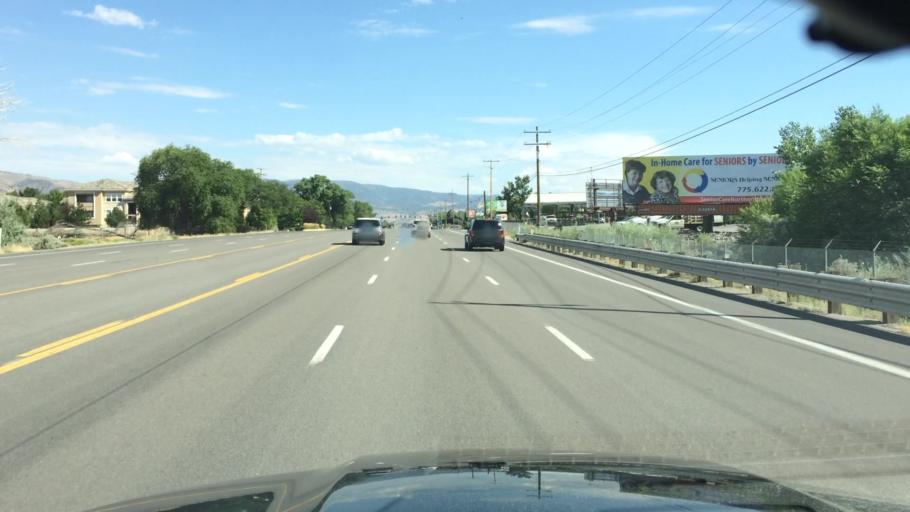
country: US
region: Nevada
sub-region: Washoe County
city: Sparks
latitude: 39.4307
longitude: -119.7643
